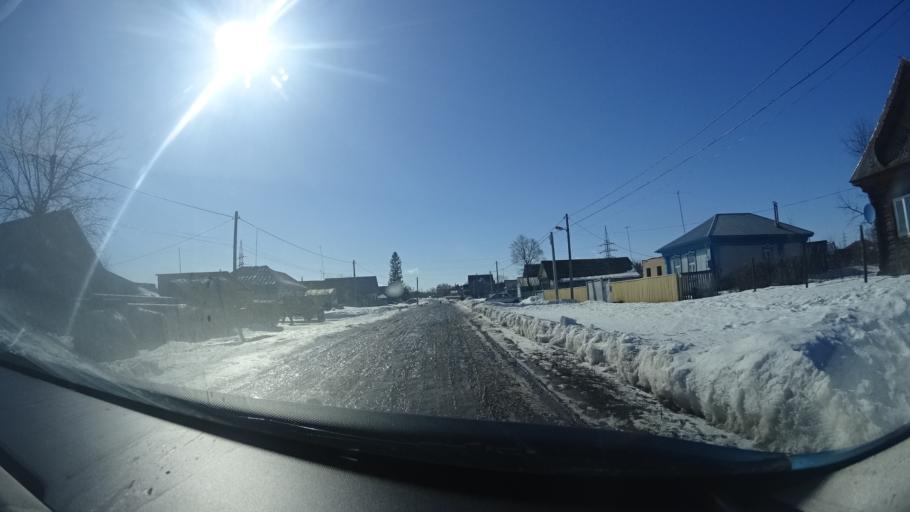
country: RU
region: Bashkortostan
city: Chishmy
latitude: 54.5794
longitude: 55.3800
